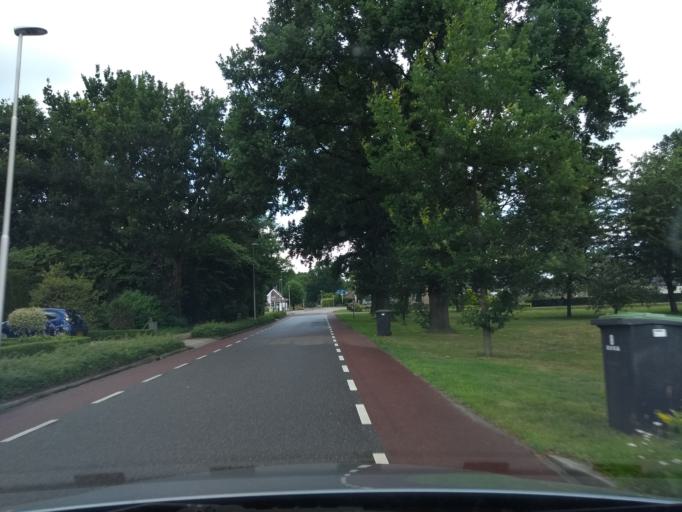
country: NL
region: Overijssel
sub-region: Gemeente Twenterand
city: Den Ham
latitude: 52.4510
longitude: 6.4166
